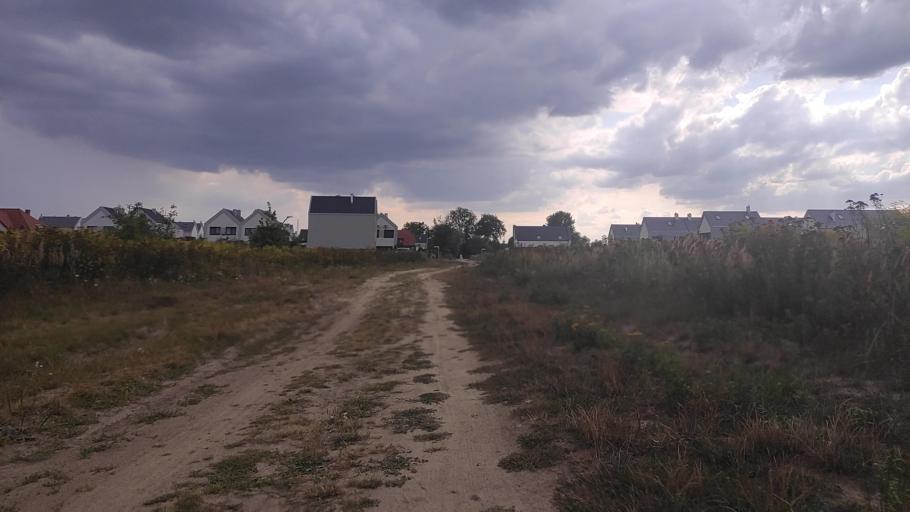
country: PL
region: Greater Poland Voivodeship
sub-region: Powiat poznanski
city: Swarzedz
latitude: 52.3922
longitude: 17.1230
